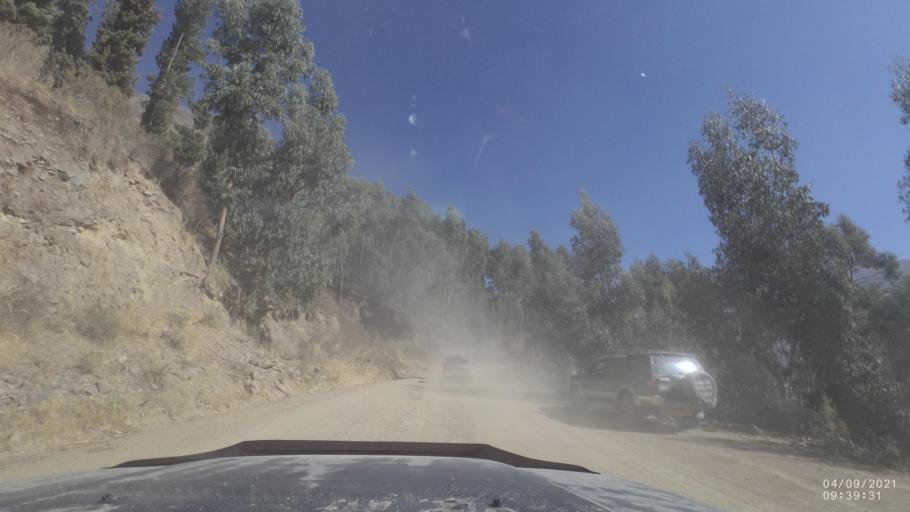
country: BO
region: Cochabamba
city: Sipe Sipe
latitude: -17.3458
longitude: -66.3852
